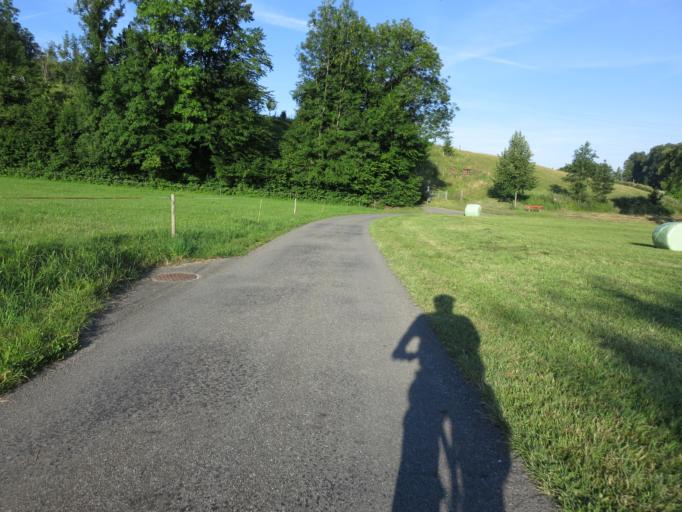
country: CH
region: Zurich
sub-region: Bezirk Hinwil
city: Bubikon
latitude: 47.2526
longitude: 8.8177
